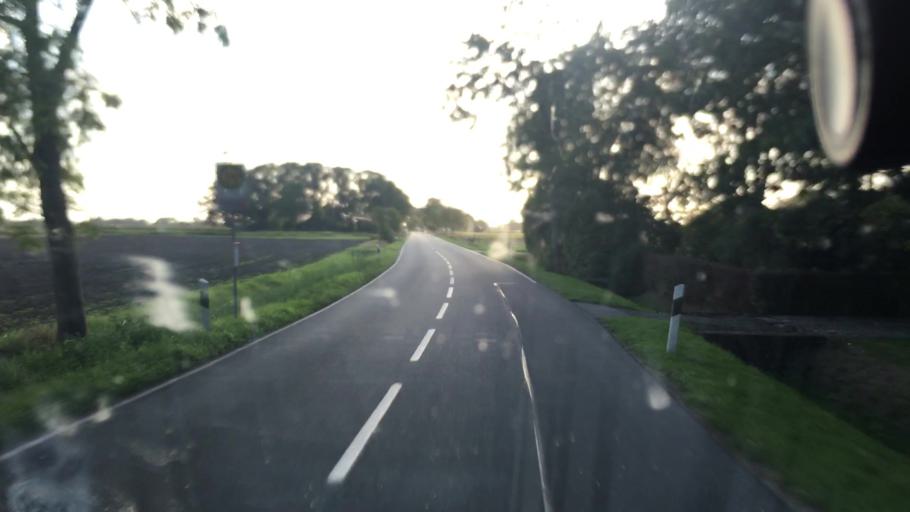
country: DE
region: Lower Saxony
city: Wittmund
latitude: 53.6432
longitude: 7.8076
